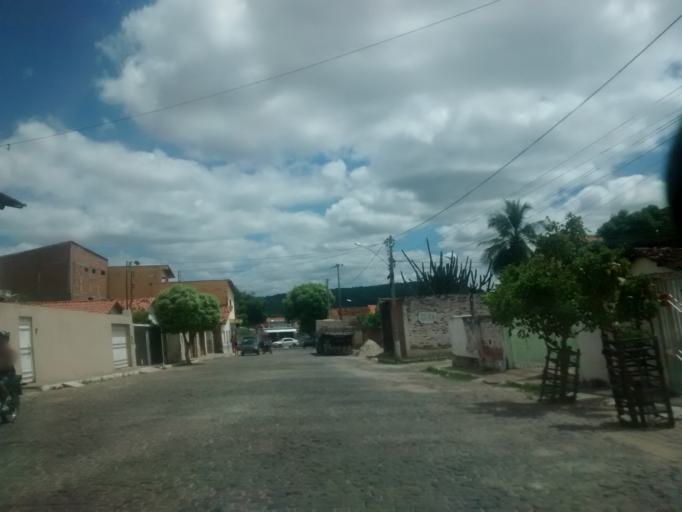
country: BR
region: Bahia
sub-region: Brumado
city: Brumado
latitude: -14.2007
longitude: -41.6691
